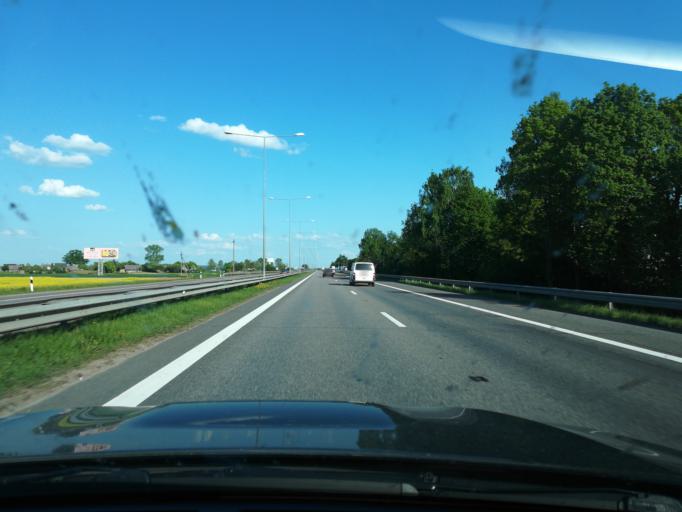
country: LT
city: Kaisiadorys
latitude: 54.8440
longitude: 24.3344
